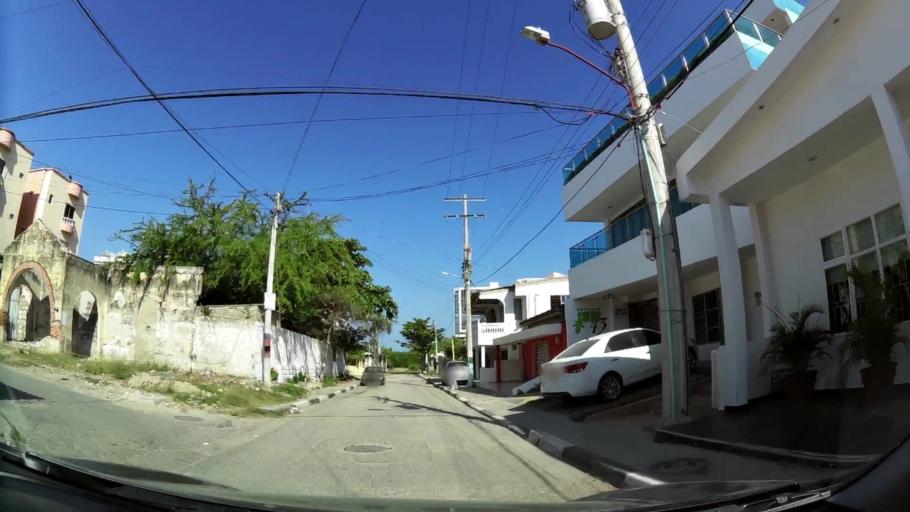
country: CO
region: Bolivar
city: Cartagena
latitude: 10.4323
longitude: -75.5362
